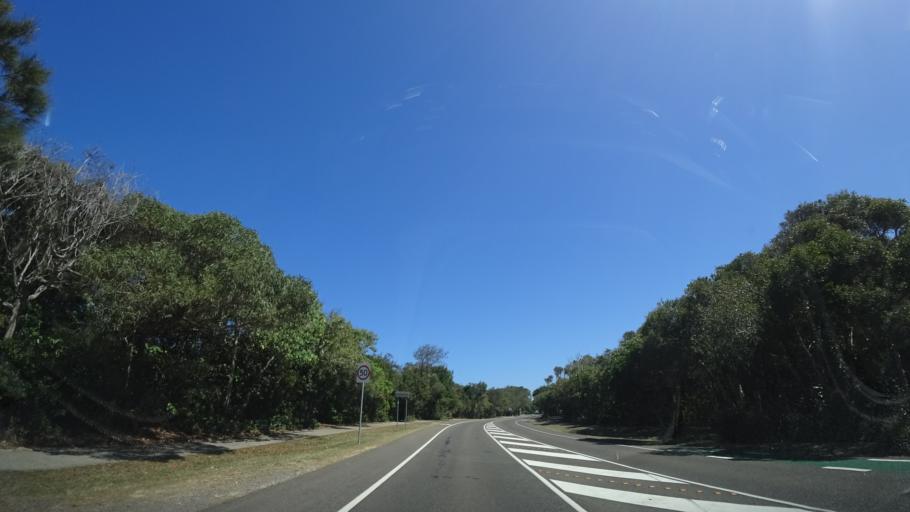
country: AU
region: Queensland
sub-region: Sunshine Coast
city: Mooloolaba
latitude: -26.6089
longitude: 153.0991
